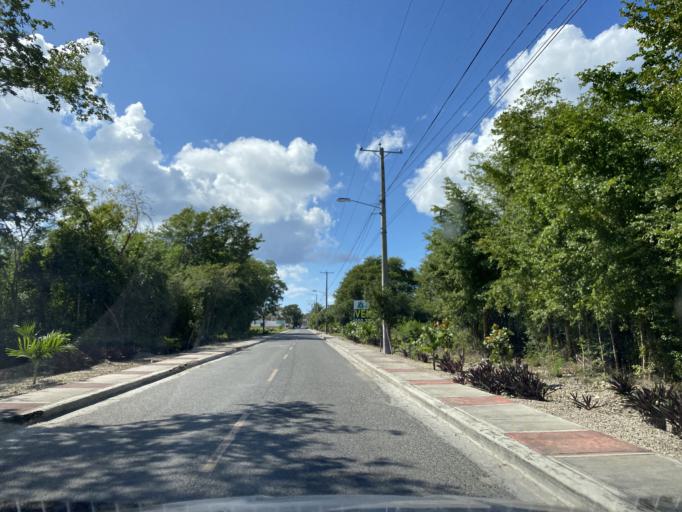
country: DO
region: La Romana
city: La Romana
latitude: 18.3532
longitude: -68.8260
